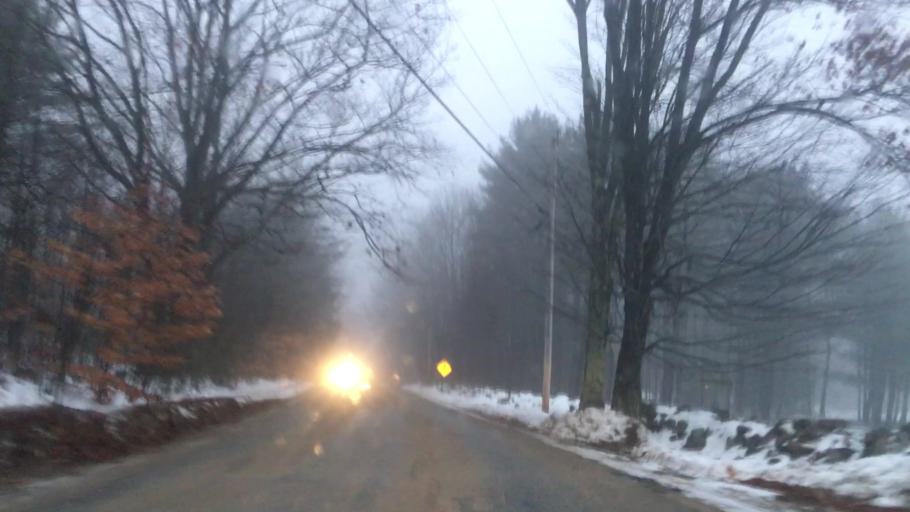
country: US
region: Maine
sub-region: Oxford County
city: Porter
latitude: 43.8217
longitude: -70.9405
